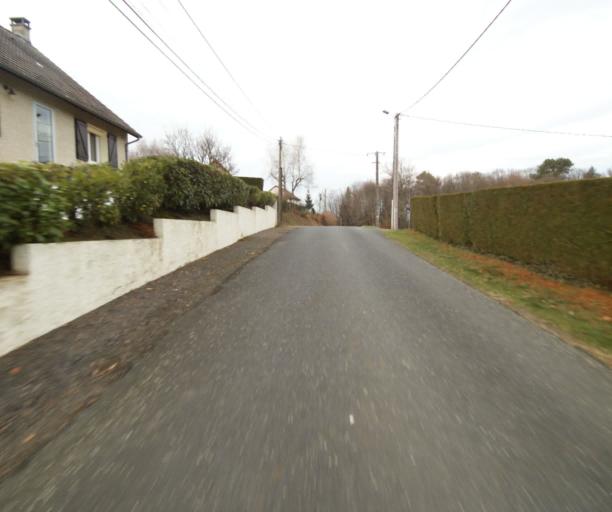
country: FR
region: Limousin
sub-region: Departement de la Correze
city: Chameyrat
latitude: 45.2404
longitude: 1.6724
